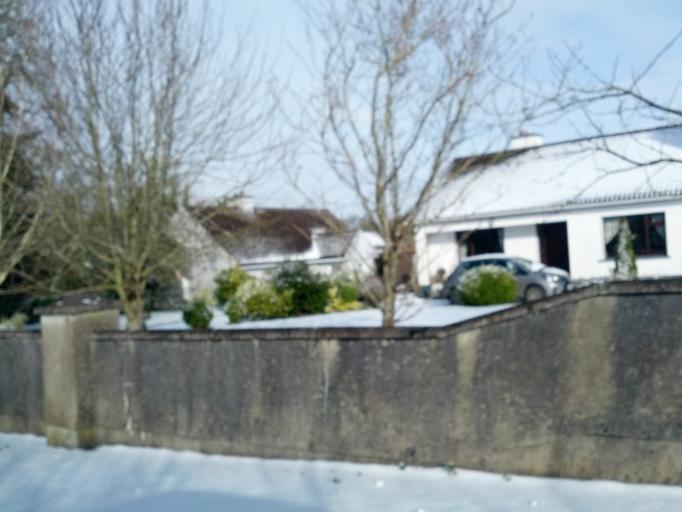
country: IE
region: Connaught
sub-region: County Galway
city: Athenry
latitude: 53.2192
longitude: -8.7629
